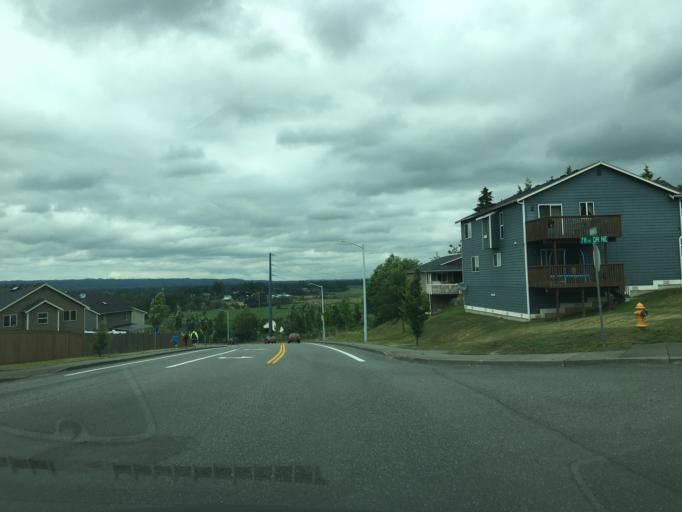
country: US
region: Washington
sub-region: Snohomish County
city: Sisco Heights
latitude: 48.0759
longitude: -122.1246
